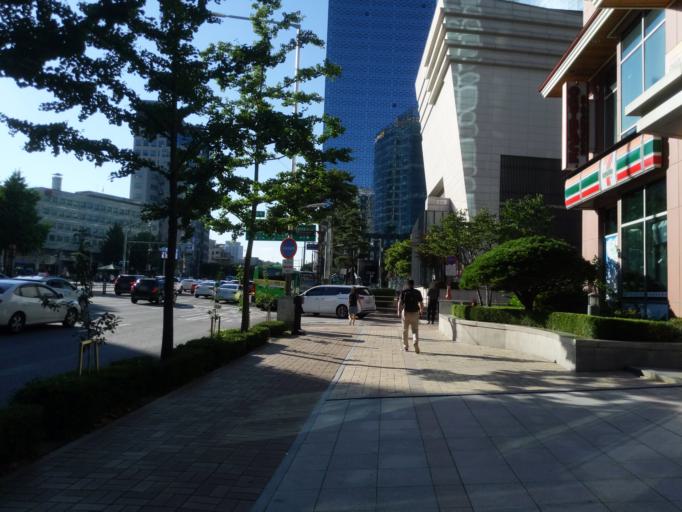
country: KR
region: Seoul
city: Seoul
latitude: 37.5649
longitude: 126.9678
